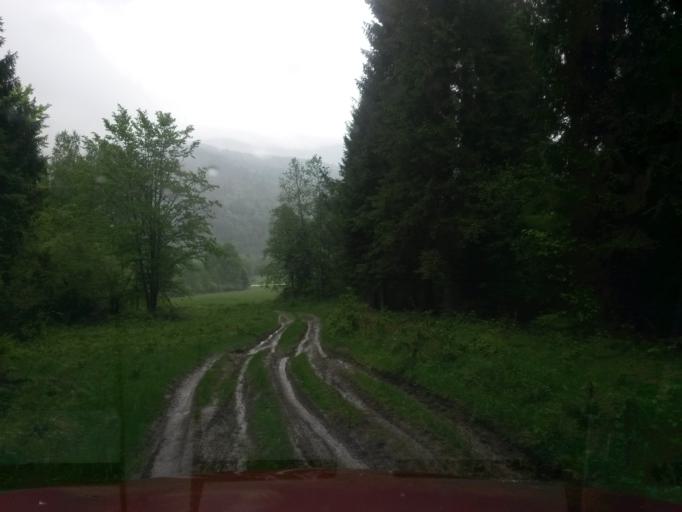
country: SK
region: Kosicky
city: Medzev
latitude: 48.7866
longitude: 20.7758
